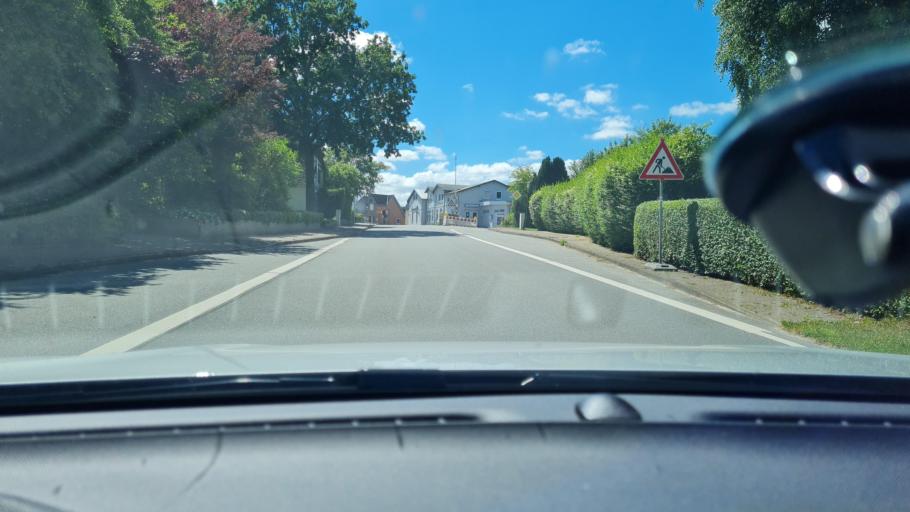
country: DE
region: Schleswig-Holstein
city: Winnemark
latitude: 54.6153
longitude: 9.9217
